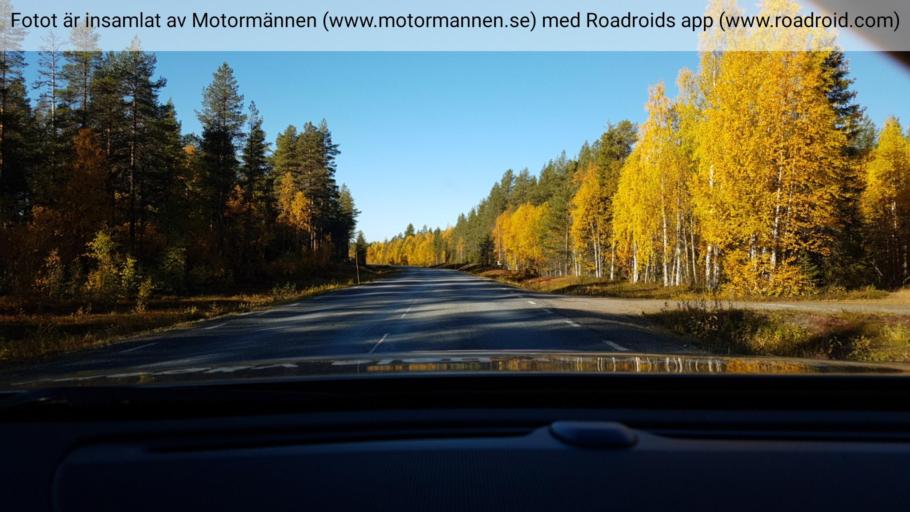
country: SE
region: Vaesterbotten
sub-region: Skelleftea Kommun
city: Storvik
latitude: 65.3857
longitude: 20.3132
